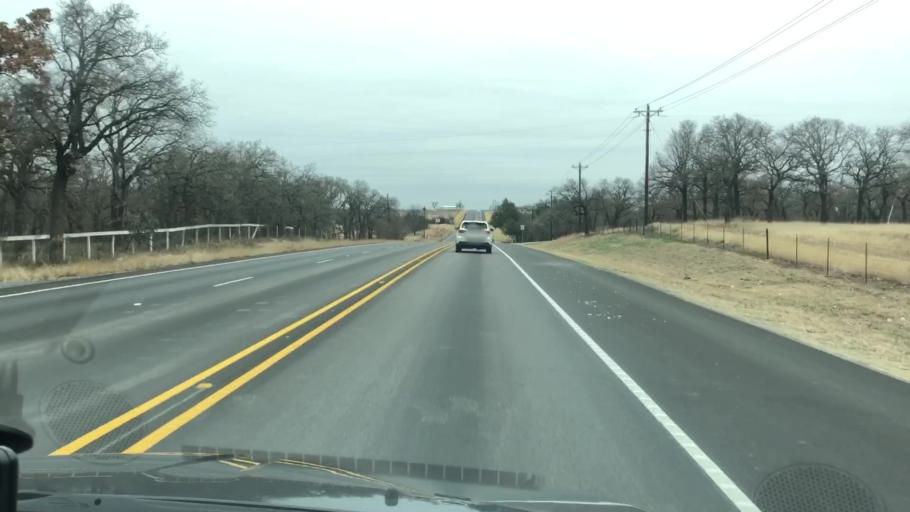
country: US
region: Texas
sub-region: Erath County
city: Stephenville
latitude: 32.2877
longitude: -98.1917
